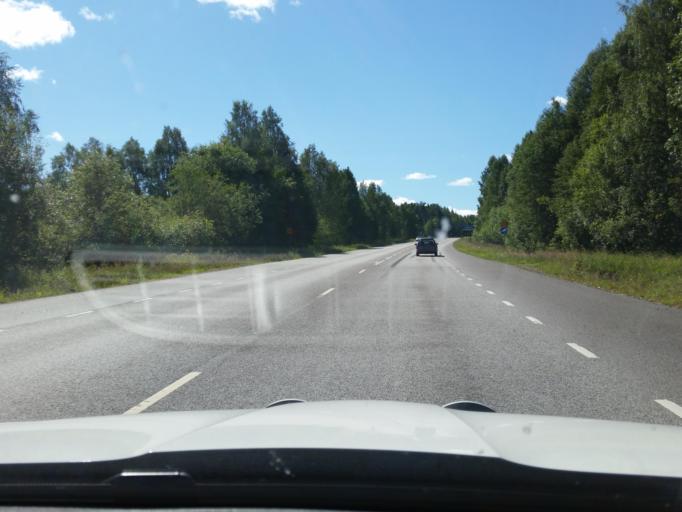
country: SE
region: Norrbotten
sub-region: Pitea Kommun
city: Pitea
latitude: 65.3017
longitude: 21.5102
